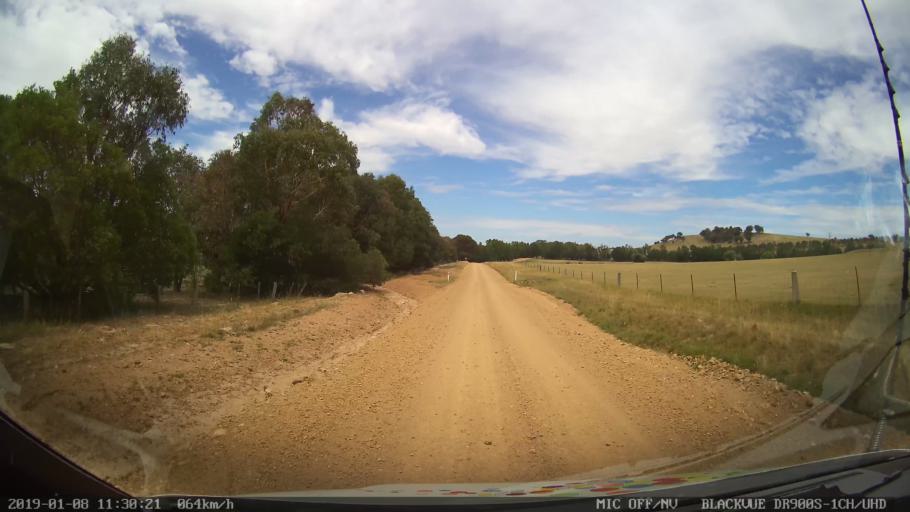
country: AU
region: New South Wales
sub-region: Guyra
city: Guyra
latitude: -30.3072
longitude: 151.5449
